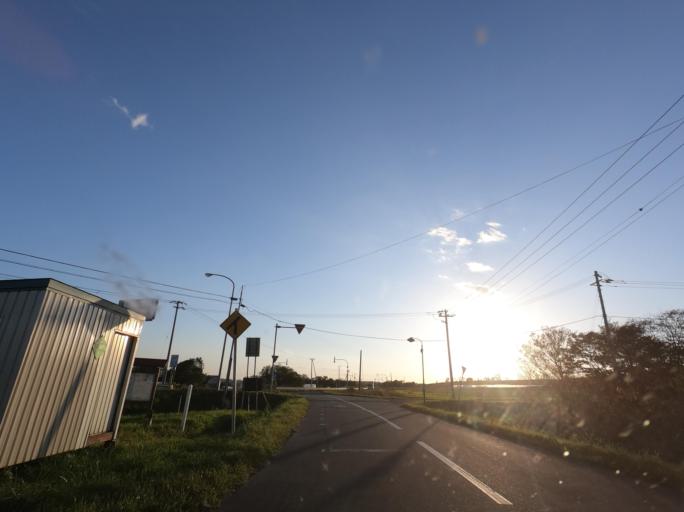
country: JP
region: Hokkaido
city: Chitose
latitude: 42.9467
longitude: 141.7684
